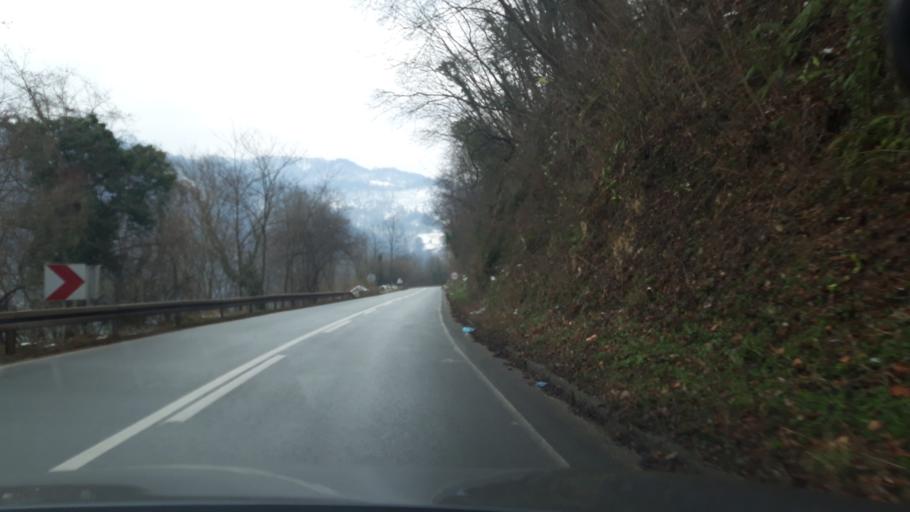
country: RS
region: Central Serbia
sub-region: Macvanski Okrug
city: Mali Zvornik
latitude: 44.3395
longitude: 19.1284
